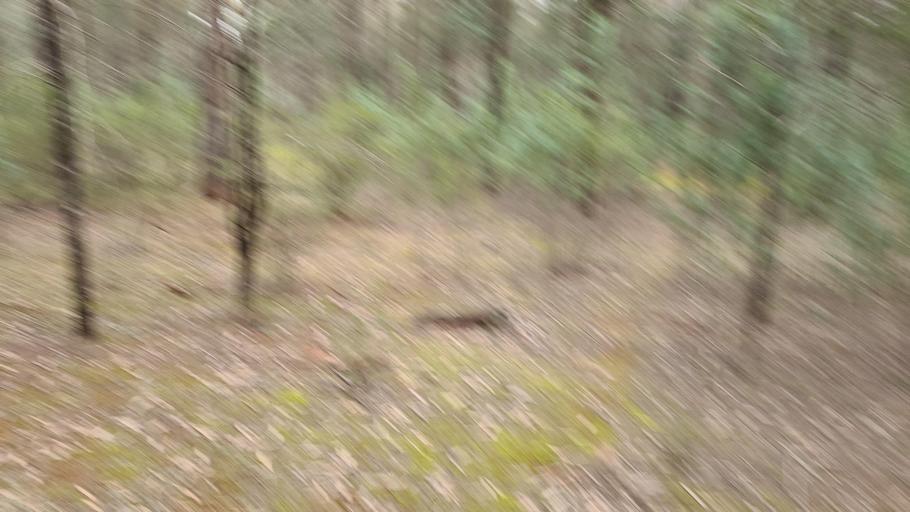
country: AU
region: New South Wales
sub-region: Coolamon
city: Coolamon
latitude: -34.8582
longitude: 146.9243
